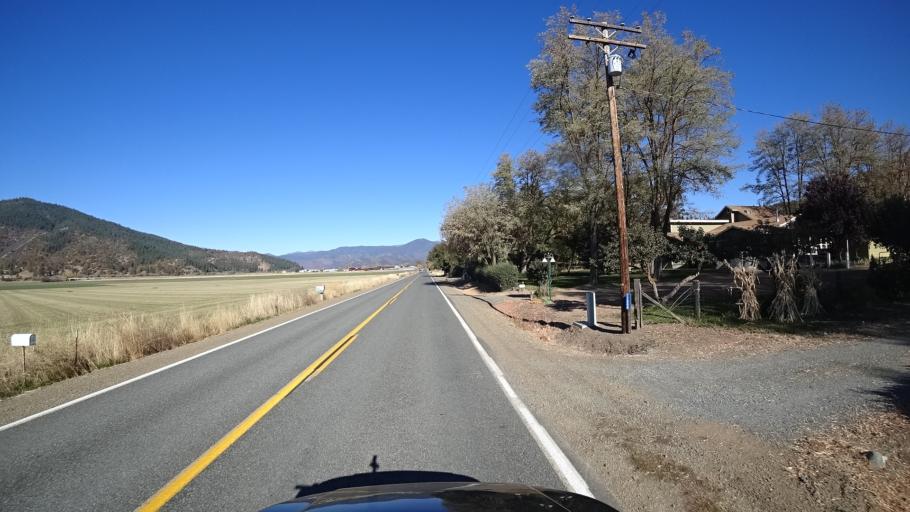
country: US
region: California
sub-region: Siskiyou County
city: Yreka
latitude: 41.5943
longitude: -122.8408
